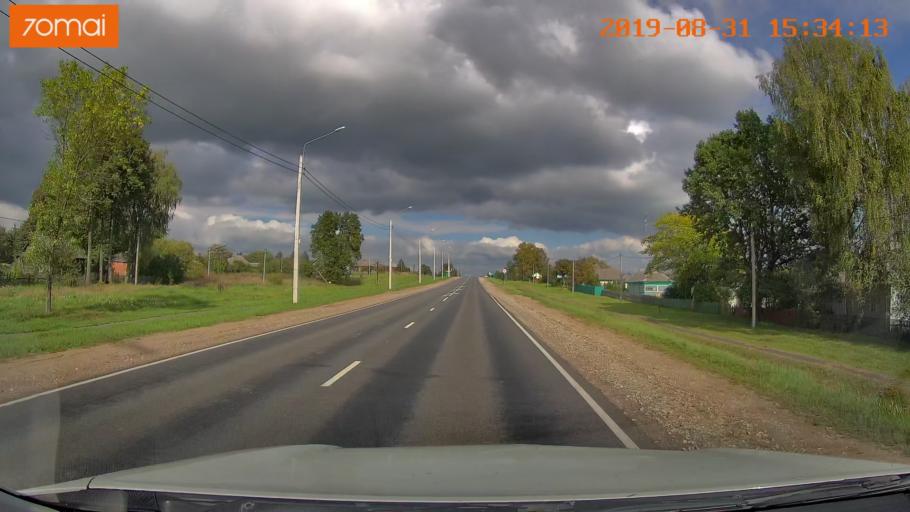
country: RU
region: Kaluga
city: Mosal'sk
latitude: 54.5994
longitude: 34.7163
